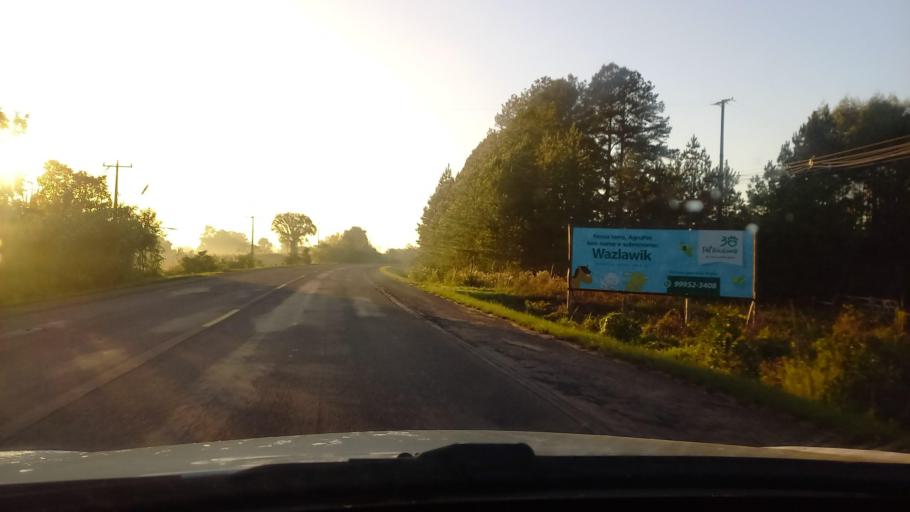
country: BR
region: Rio Grande do Sul
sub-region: Candelaria
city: Candelaria
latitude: -29.6807
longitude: -52.8241
